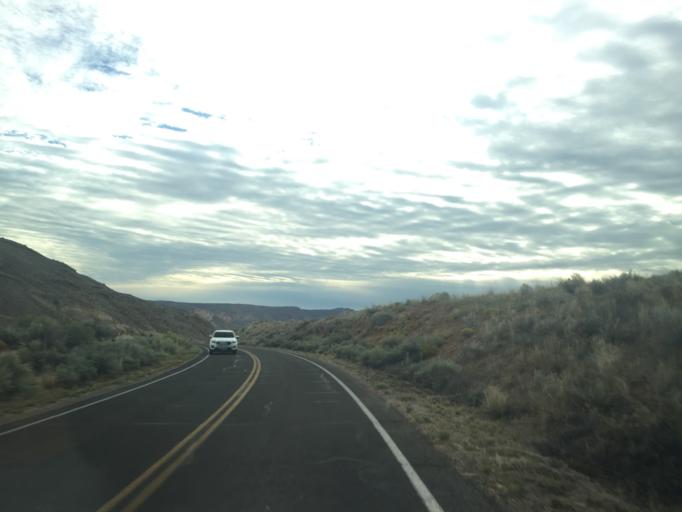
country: US
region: Utah
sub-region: Grand County
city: Moab
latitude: 38.7317
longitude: -109.5484
